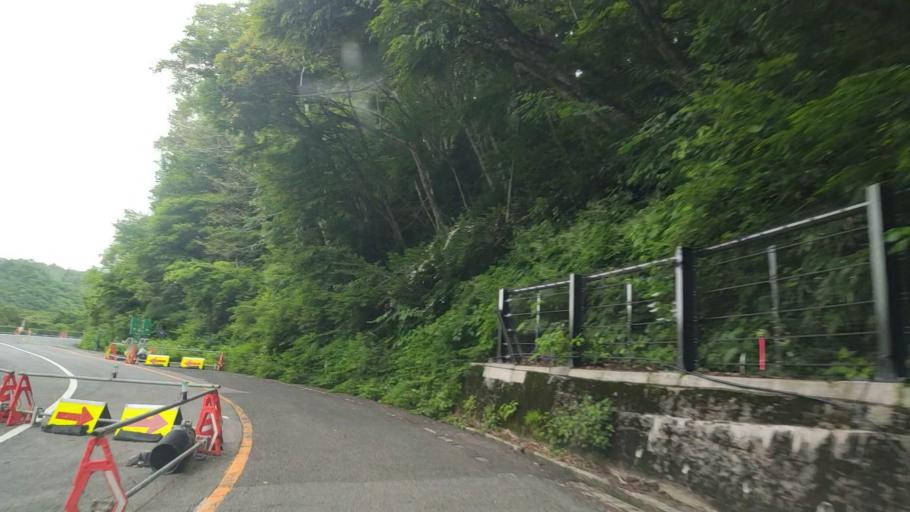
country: JP
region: Tottori
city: Yonago
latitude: 35.3494
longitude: 133.5487
